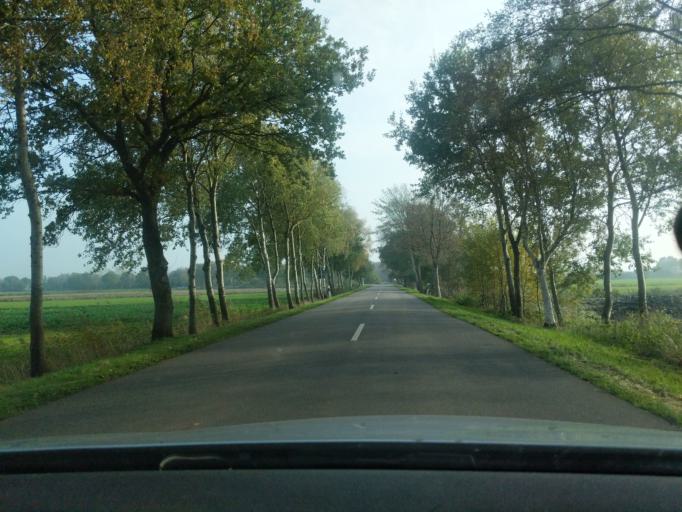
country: DE
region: Lower Saxony
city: Stinstedt
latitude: 53.6507
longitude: 8.9898
